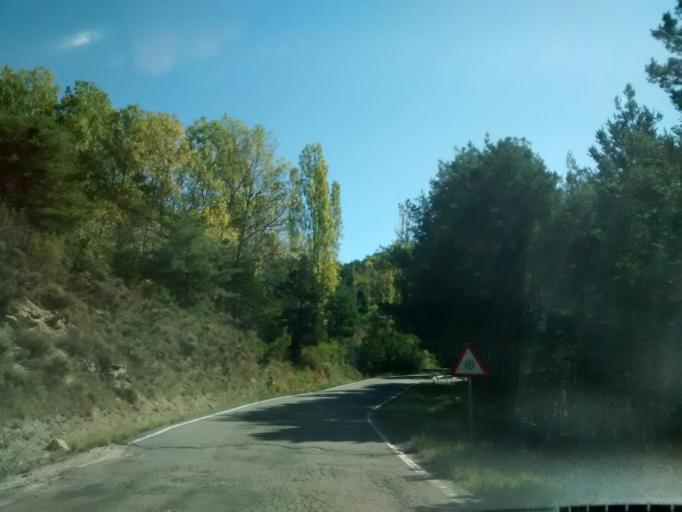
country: ES
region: Aragon
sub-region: Provincia de Huesca
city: Jaca
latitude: 42.5121
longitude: -0.5578
